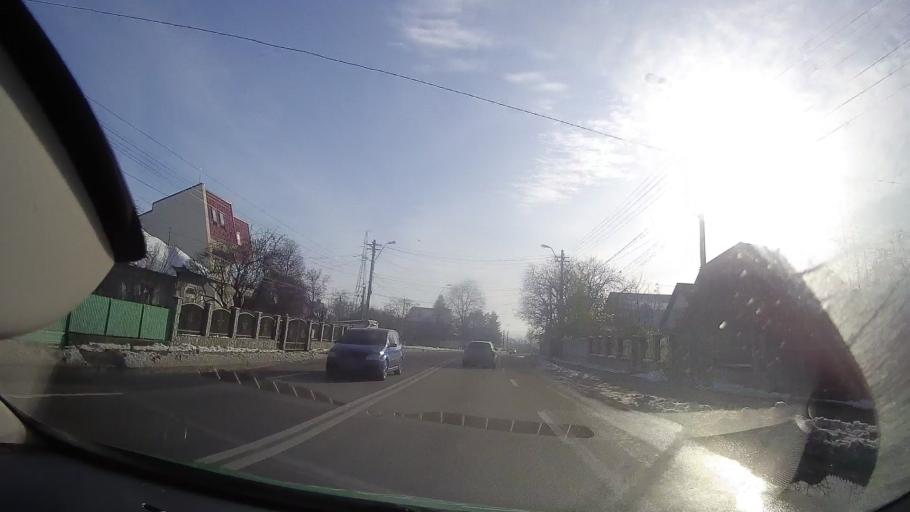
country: RO
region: Neamt
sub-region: Comuna Dobreni
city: Dobreni
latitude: 46.9502
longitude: 26.3844
